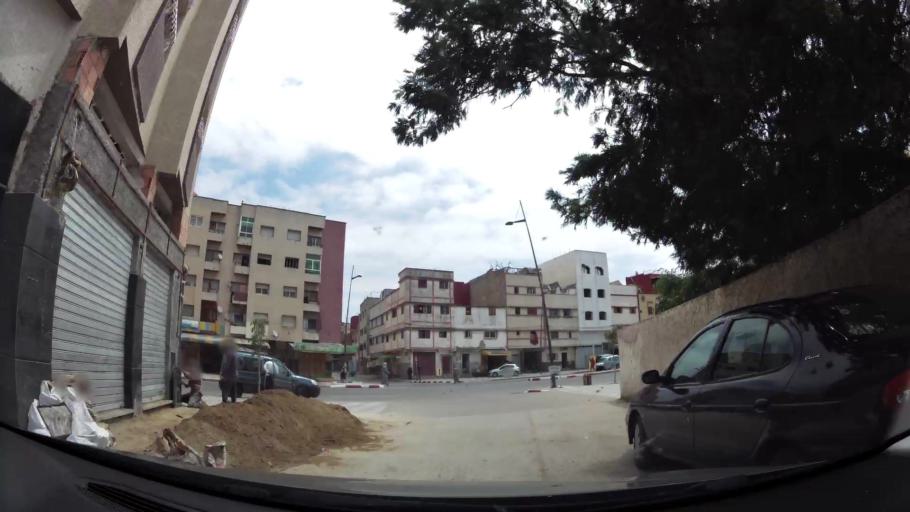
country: MA
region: Rabat-Sale-Zemmour-Zaer
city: Sale
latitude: 34.0582
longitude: -6.7787
